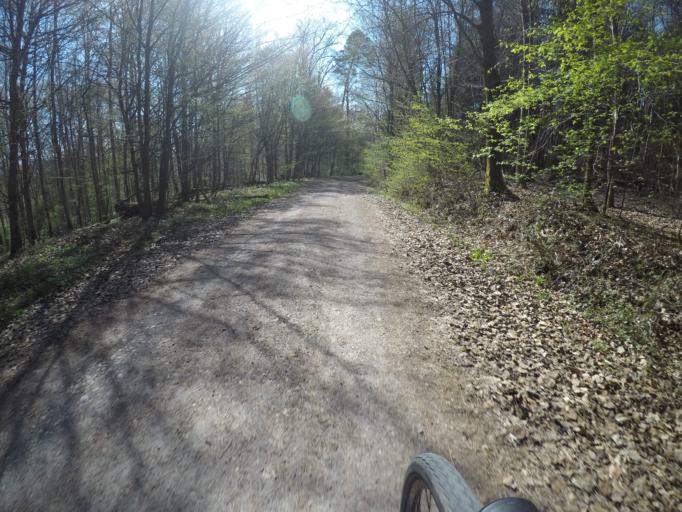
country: DE
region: Baden-Wuerttemberg
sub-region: Regierungsbezirk Stuttgart
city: Schlaitdorf
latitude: 48.6252
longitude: 9.2208
